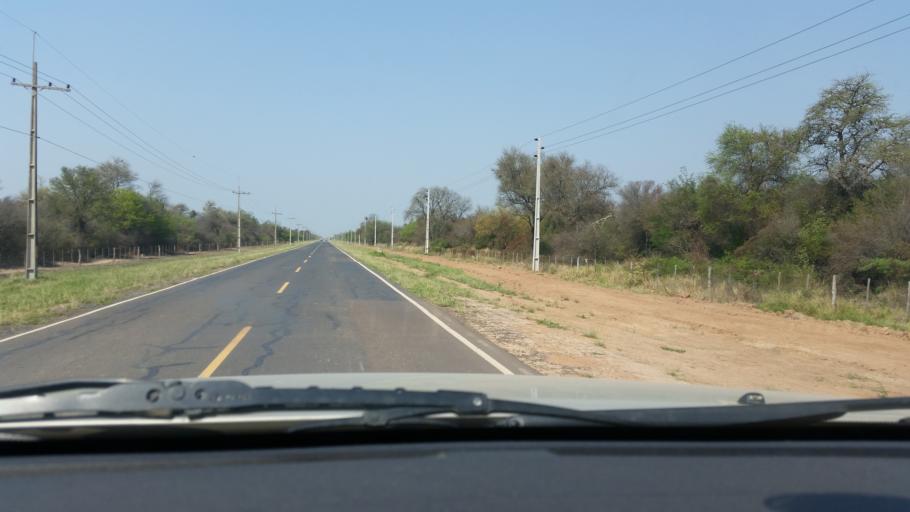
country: PY
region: Boqueron
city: Colonia Neuland
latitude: -22.5193
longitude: -60.0732
